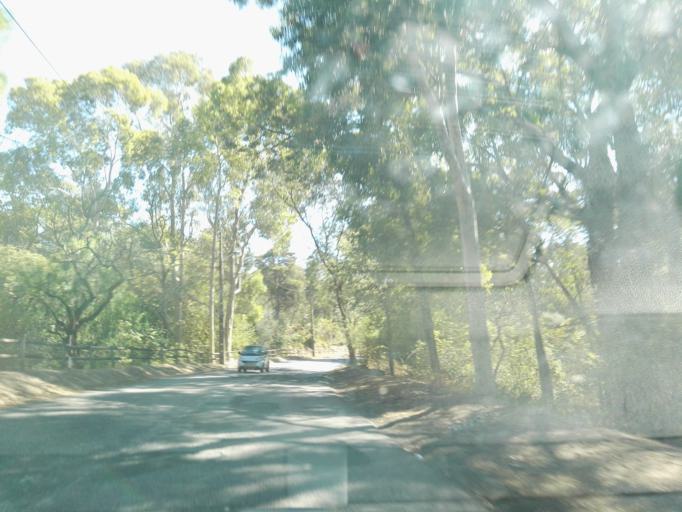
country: PT
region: Lisbon
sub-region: Oeiras
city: Alges
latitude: 38.7268
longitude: -9.1999
